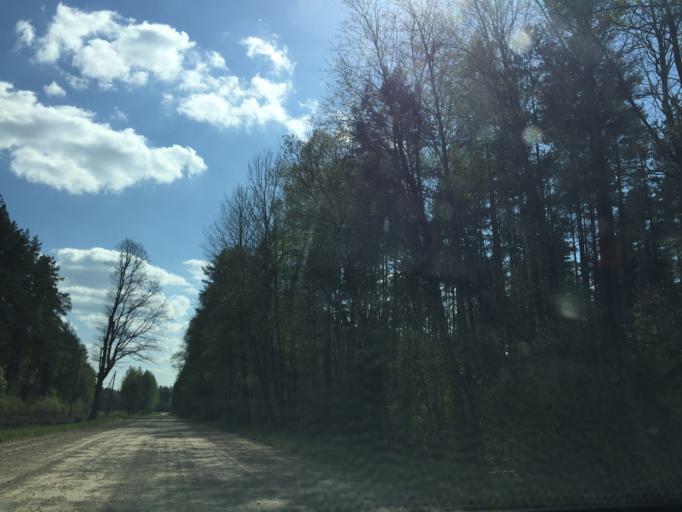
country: LV
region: Vecumnieki
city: Vecumnieki
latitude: 56.4819
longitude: 24.5348
